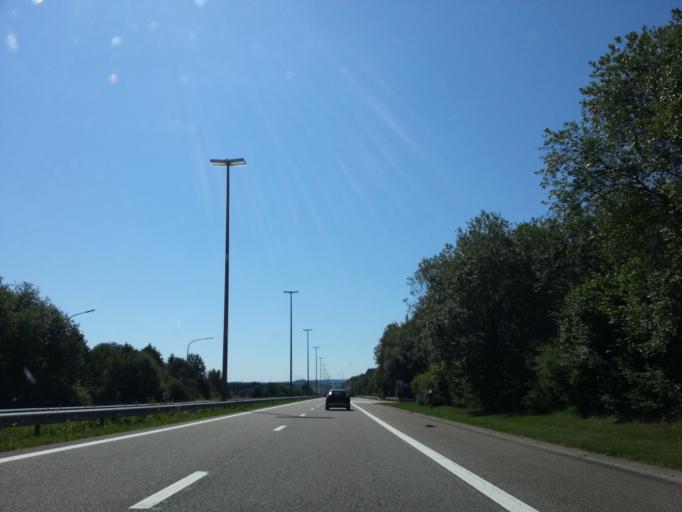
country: BE
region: Wallonia
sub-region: Province de Liege
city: Saint-Vith
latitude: 50.2517
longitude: 6.1706
